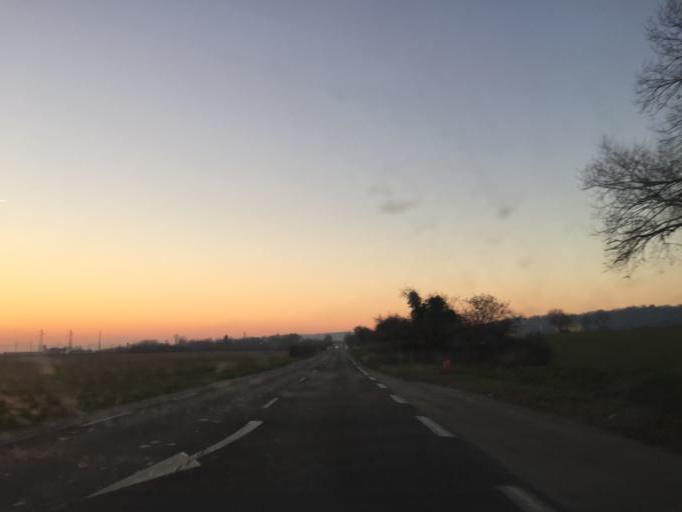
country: FR
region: Rhone-Alpes
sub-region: Departement de l'Ain
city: Balan
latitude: 45.8501
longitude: 5.0961
